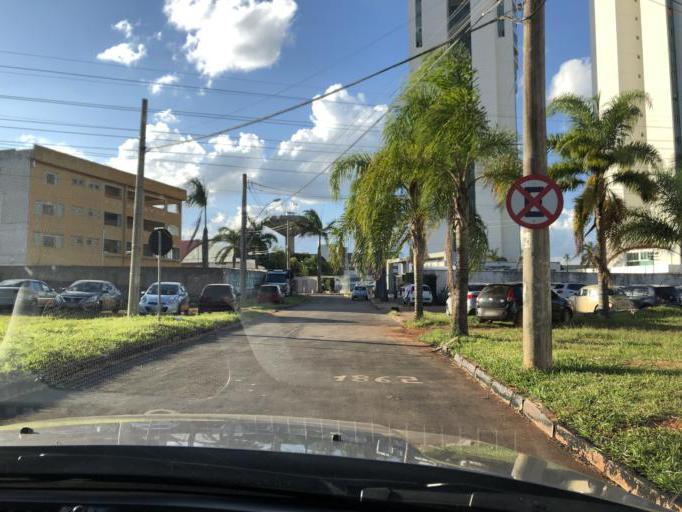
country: BR
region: Federal District
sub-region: Brasilia
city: Brasilia
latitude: -15.8543
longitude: -48.0378
